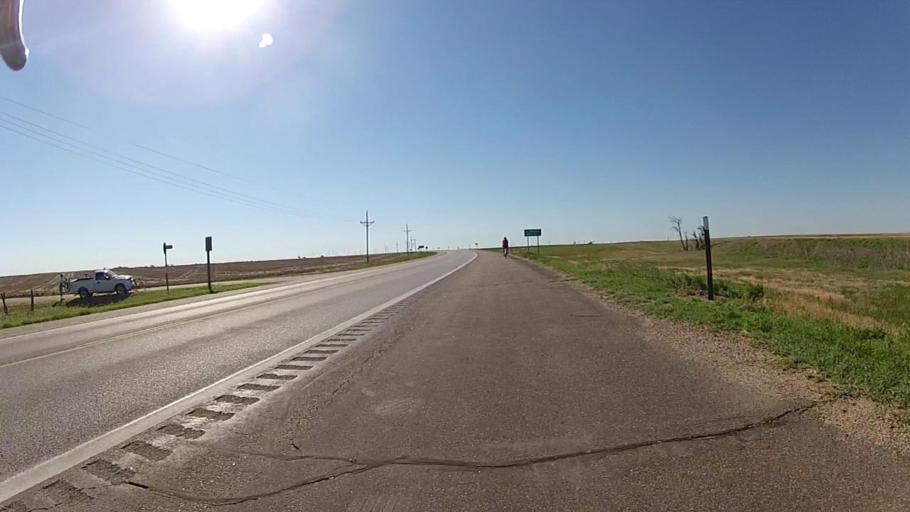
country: US
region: Kansas
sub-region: Ford County
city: Dodge City
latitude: 37.5883
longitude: -99.6856
